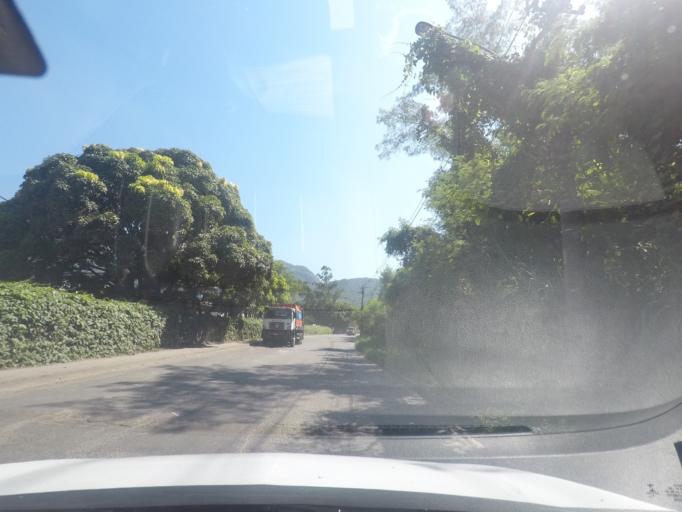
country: BR
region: Rio de Janeiro
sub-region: Nilopolis
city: Nilopolis
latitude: -22.9859
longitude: -43.4526
